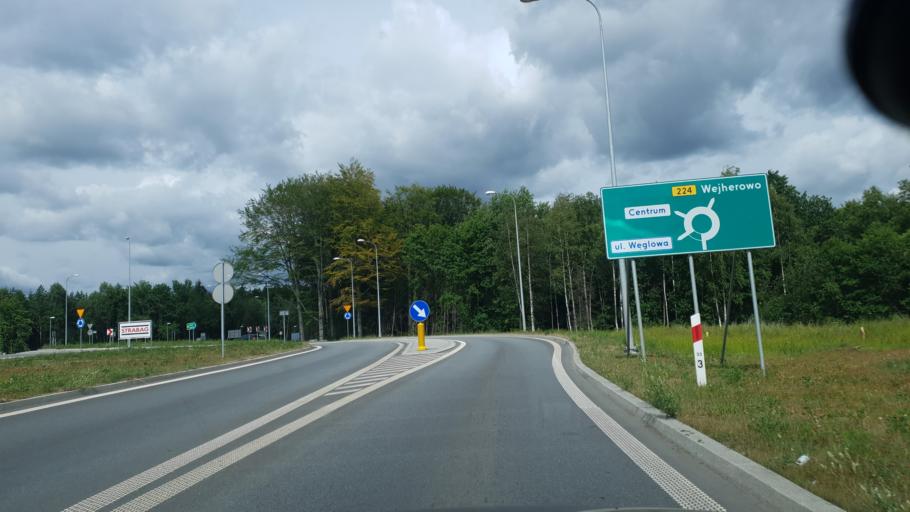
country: PL
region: Pomeranian Voivodeship
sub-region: Powiat kartuski
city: Kartuzy
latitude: 54.3385
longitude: 18.2103
